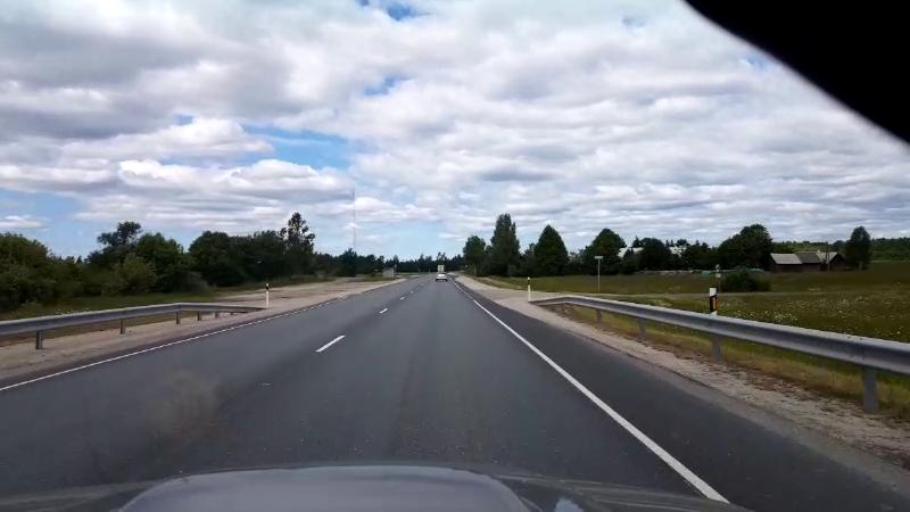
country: EE
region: Raplamaa
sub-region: Maerjamaa vald
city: Marjamaa
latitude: 58.7728
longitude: 24.4149
